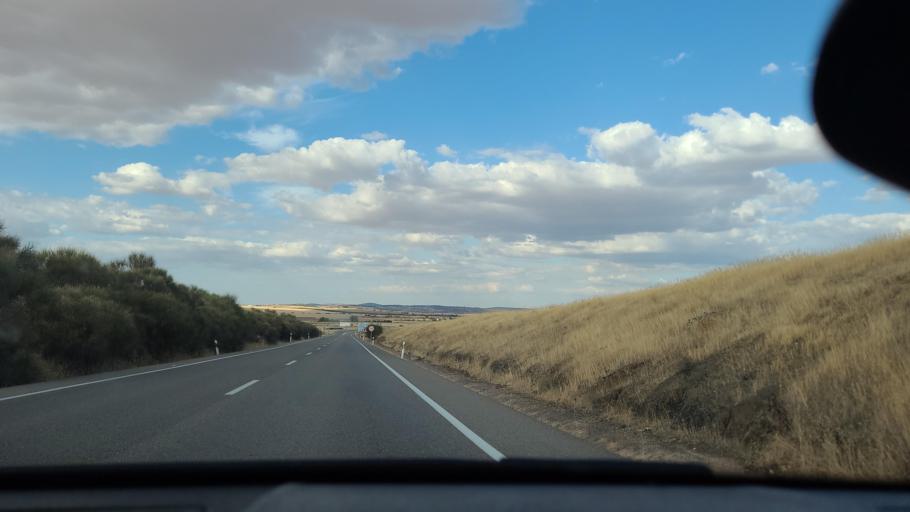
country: ES
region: Andalusia
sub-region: Province of Cordoba
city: Fuente Obejuna
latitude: 38.2725
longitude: -5.4294
